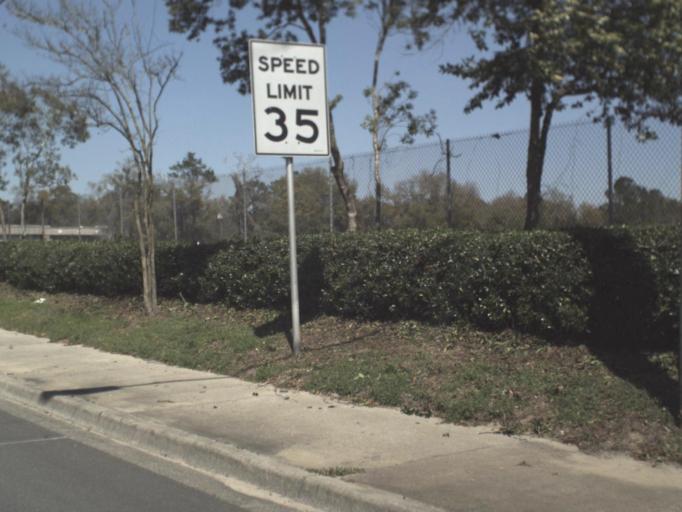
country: US
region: Florida
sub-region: Leon County
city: Tallahassee
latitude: 30.3989
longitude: -84.2802
